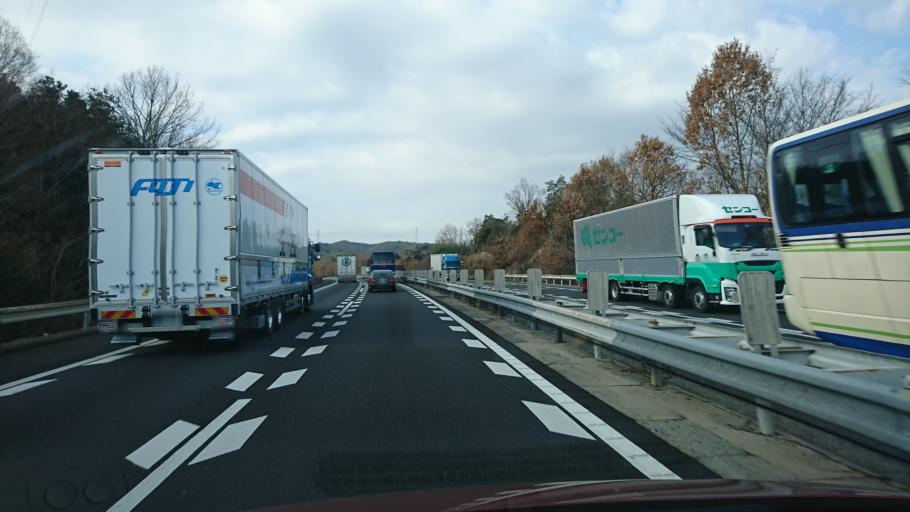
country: JP
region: Hyogo
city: Aioi
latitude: 34.8061
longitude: 134.4432
